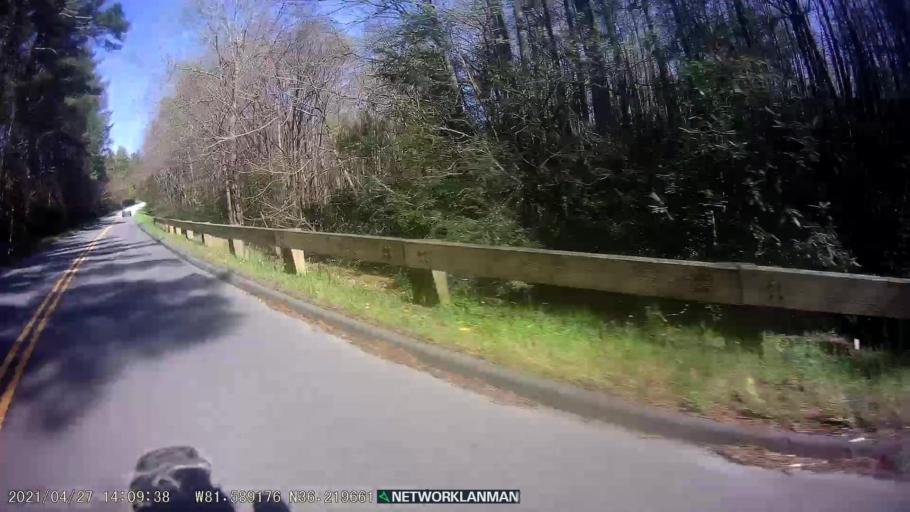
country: US
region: North Carolina
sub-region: Watauga County
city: Boone
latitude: 36.2196
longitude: -81.5889
